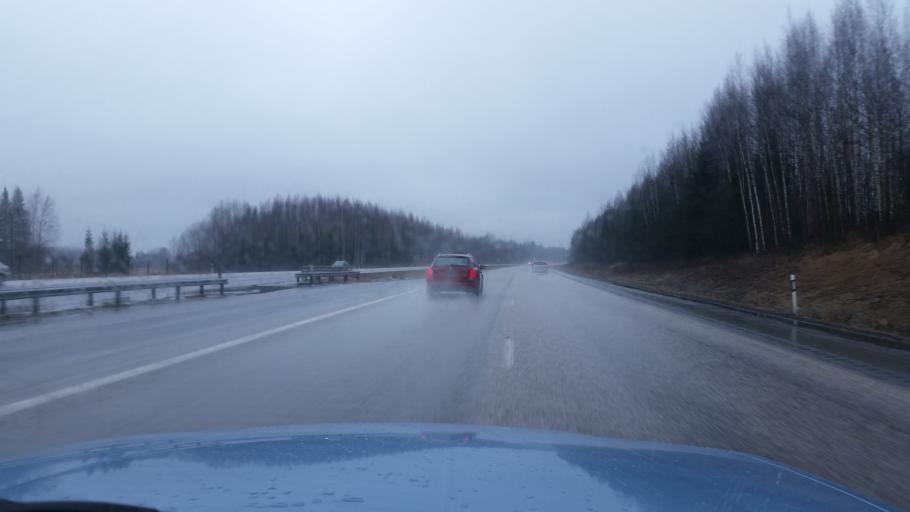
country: FI
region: Haeme
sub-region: Riihimaeki
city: Riihimaeki
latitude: 60.7253
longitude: 24.7283
